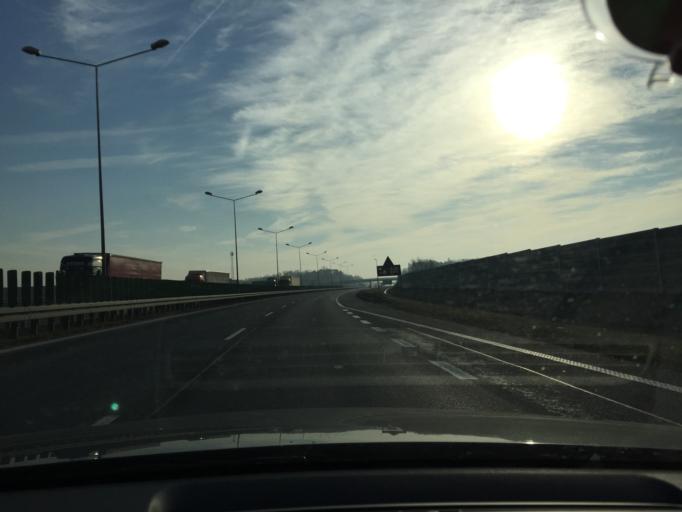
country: PL
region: Silesian Voivodeship
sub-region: Powiat gliwicki
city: Sosnicowice
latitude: 50.3433
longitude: 18.5426
